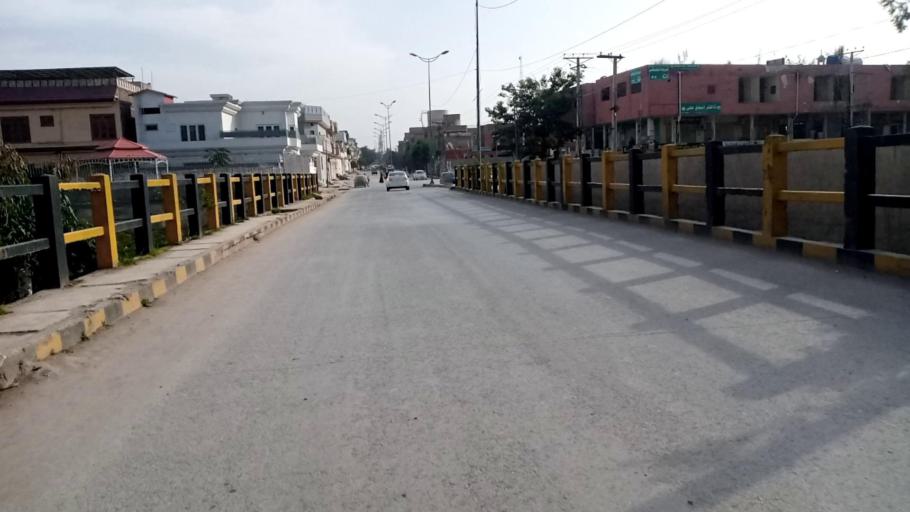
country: PK
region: Khyber Pakhtunkhwa
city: Peshawar
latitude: 33.9949
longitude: 71.4526
